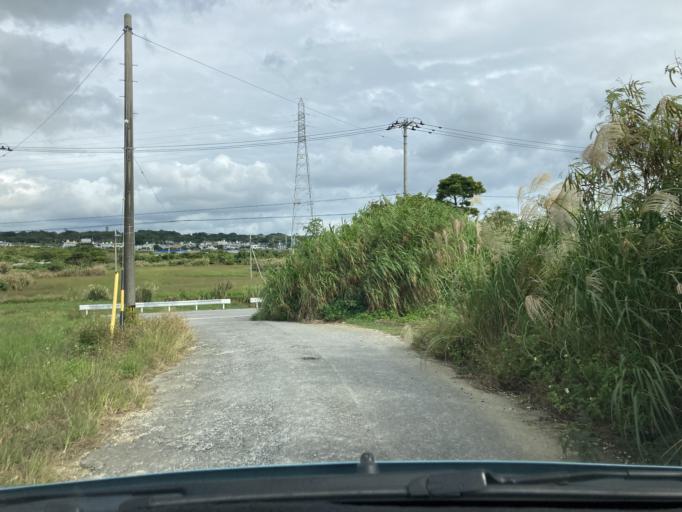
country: JP
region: Okinawa
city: Itoman
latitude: 26.1157
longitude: 127.6874
